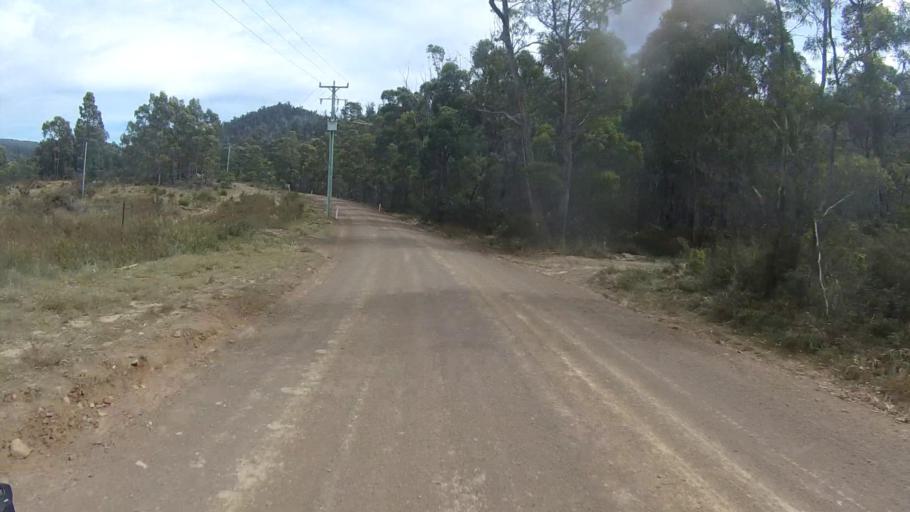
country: AU
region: Tasmania
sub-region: Sorell
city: Sorell
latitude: -42.7546
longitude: 147.7999
